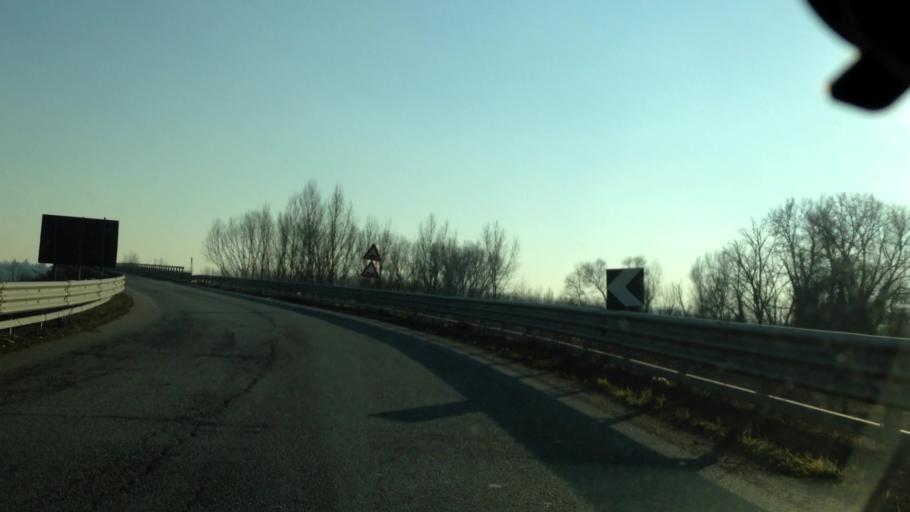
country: IT
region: Piedmont
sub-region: Provincia di Alessandria
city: Felizzano
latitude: 44.8919
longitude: 8.4382
